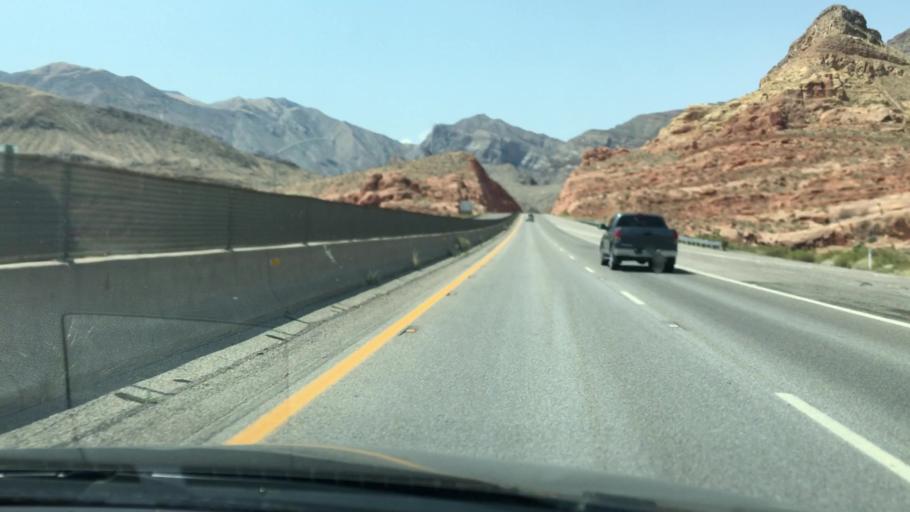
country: US
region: Arizona
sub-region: Mohave County
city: Beaver Dam
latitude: 36.9519
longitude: -113.8001
